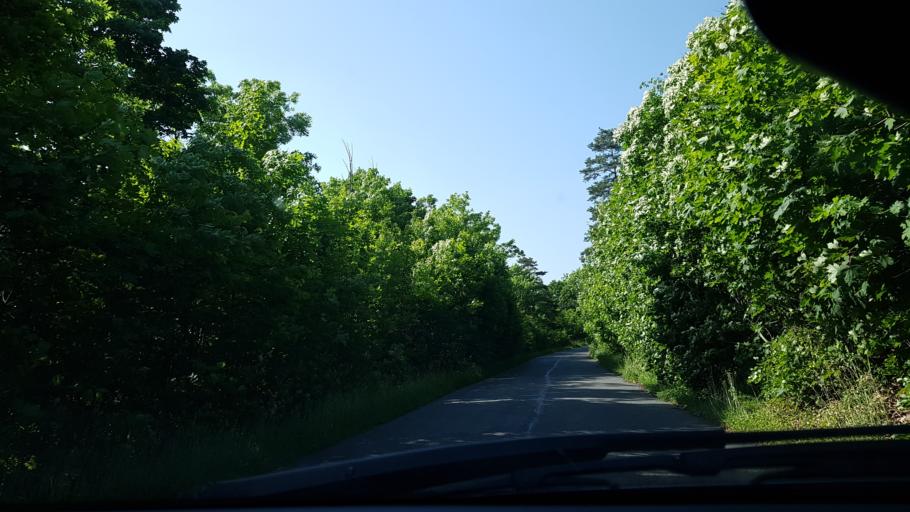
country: PL
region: Lower Silesian Voivodeship
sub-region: Powiat zabkowicki
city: Budzow
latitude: 50.5346
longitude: 16.6621
